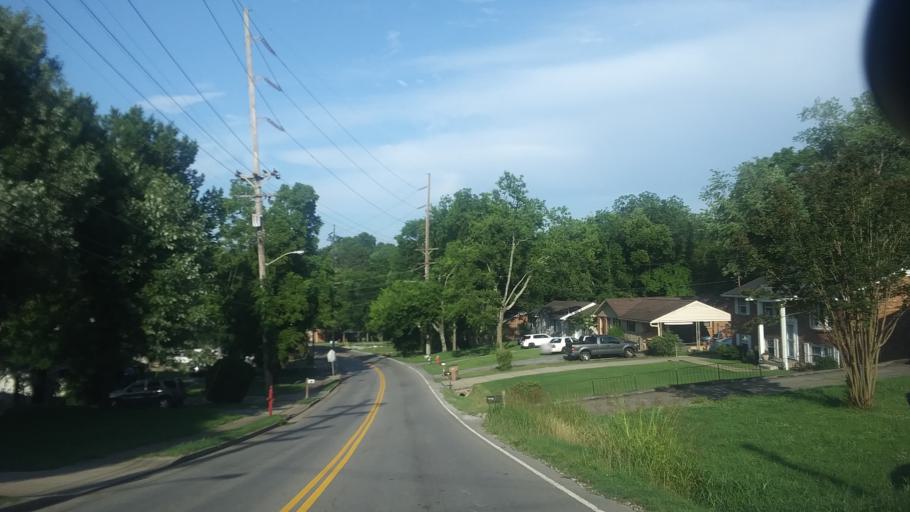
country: US
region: Tennessee
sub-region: Davidson County
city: Oak Hill
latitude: 36.0789
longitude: -86.7068
